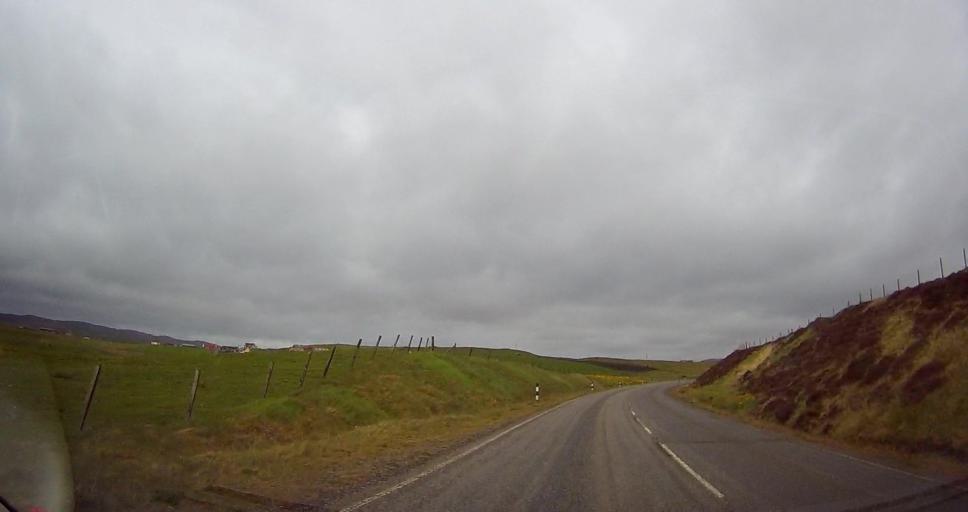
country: GB
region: Scotland
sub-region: Shetland Islands
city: Lerwick
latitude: 60.3714
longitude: -1.3340
